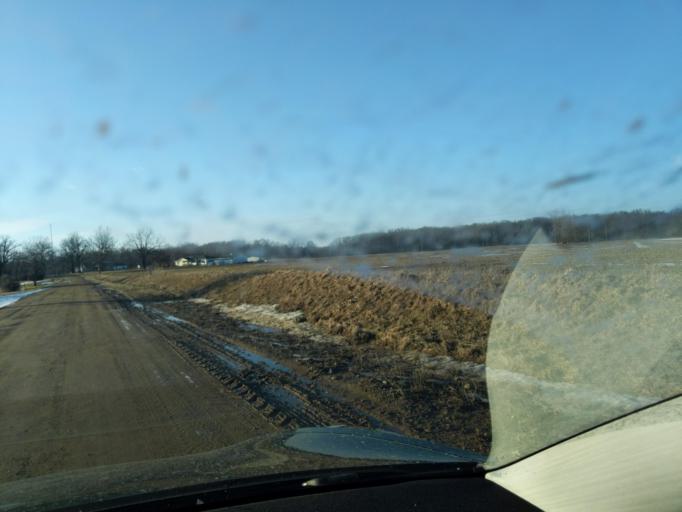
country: US
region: Michigan
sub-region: Ingham County
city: Stockbridge
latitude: 42.5286
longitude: -84.2645
